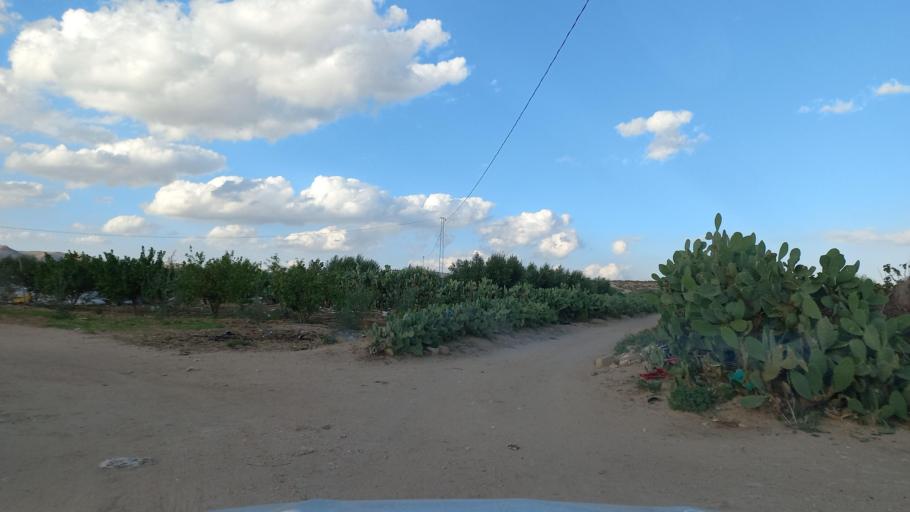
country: TN
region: Al Qasrayn
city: Sbiba
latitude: 35.3862
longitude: 9.0526
